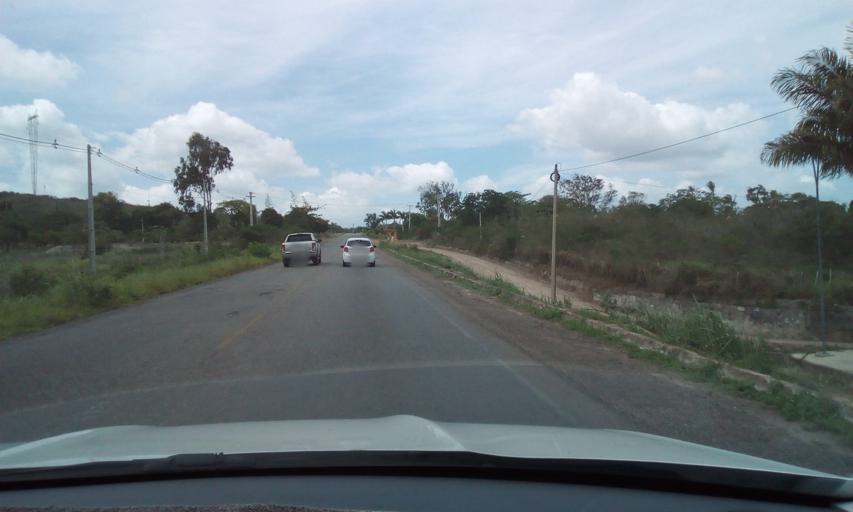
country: BR
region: Pernambuco
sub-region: Bezerros
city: Bezerros
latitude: -8.2814
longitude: -35.7424
